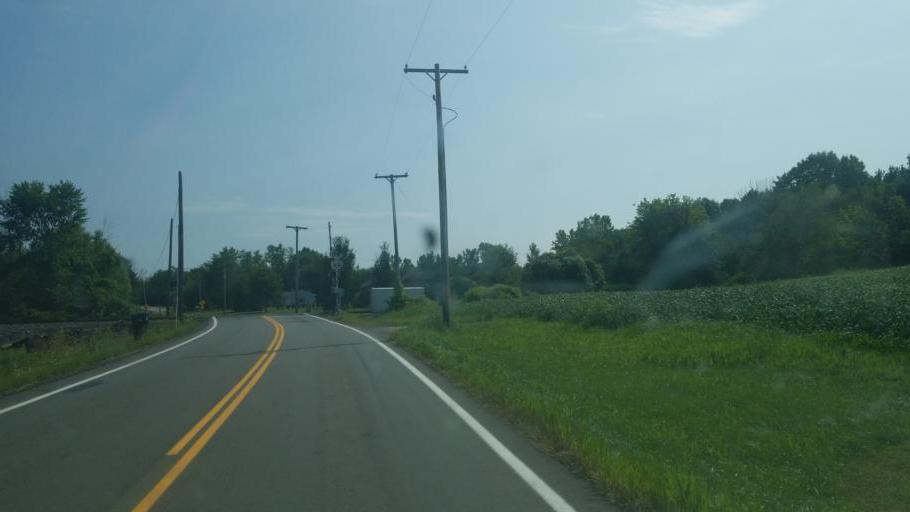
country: US
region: Ohio
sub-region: Richland County
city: Shelby
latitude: 40.8030
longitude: -82.6560
